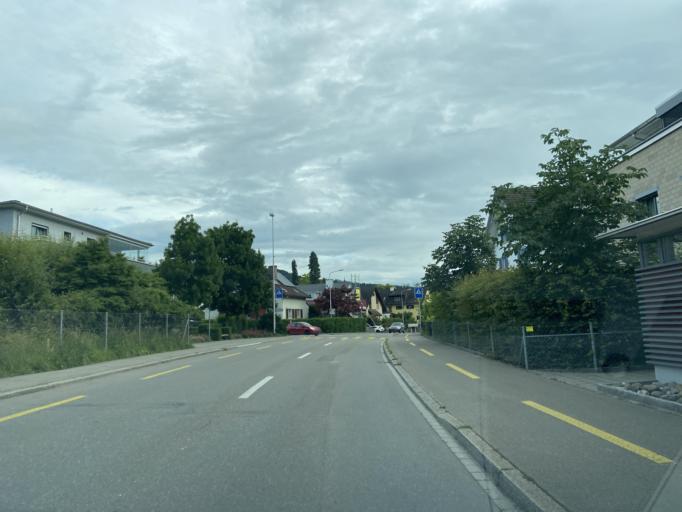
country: CH
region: Thurgau
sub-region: Muenchwilen District
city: Aadorf
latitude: 47.4898
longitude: 8.9045
